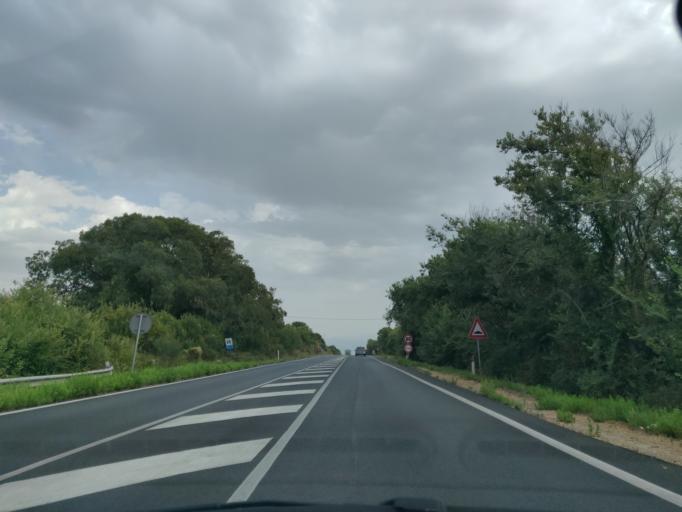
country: IT
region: Latium
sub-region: Citta metropolitana di Roma Capitale
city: Santa Marinella
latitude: 42.0314
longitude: 11.9357
